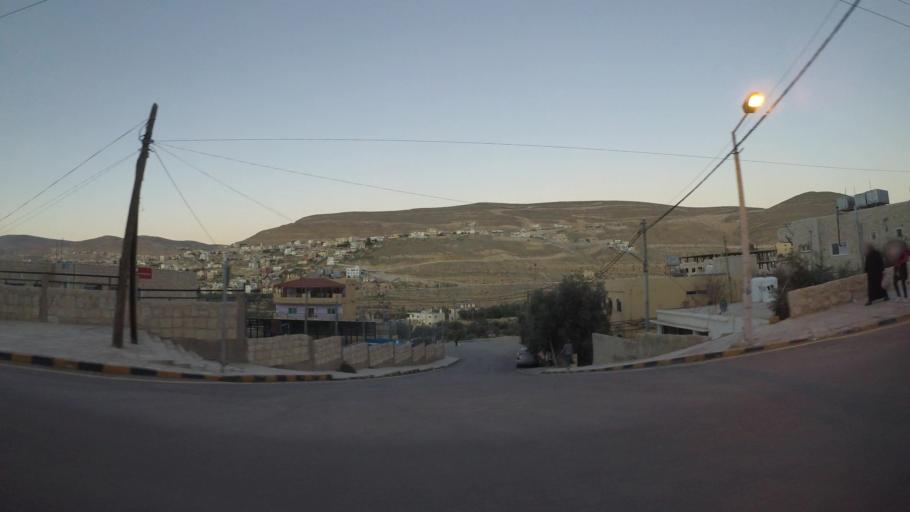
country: JO
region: Ma'an
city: Petra
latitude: 30.3126
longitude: 35.4785
